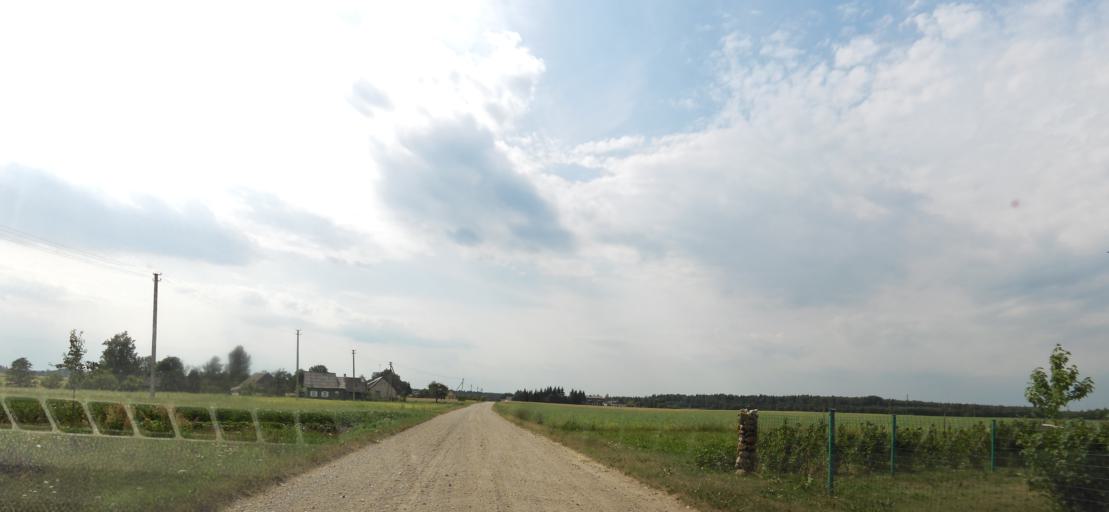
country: LT
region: Panevezys
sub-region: Birzai
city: Birzai
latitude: 56.1835
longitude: 24.9954
